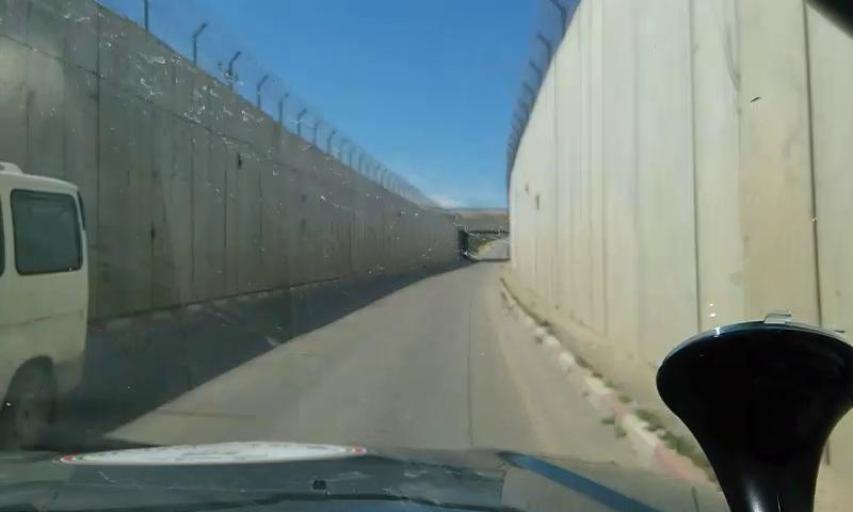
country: PS
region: West Bank
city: Biddu
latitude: 31.8387
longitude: 35.1589
